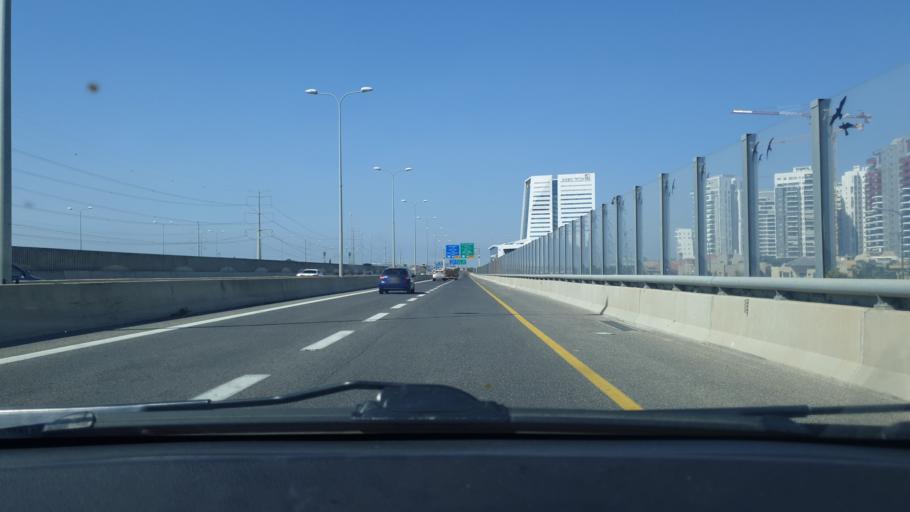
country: IL
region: Central District
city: Ness Ziona
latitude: 31.9474
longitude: 34.8087
